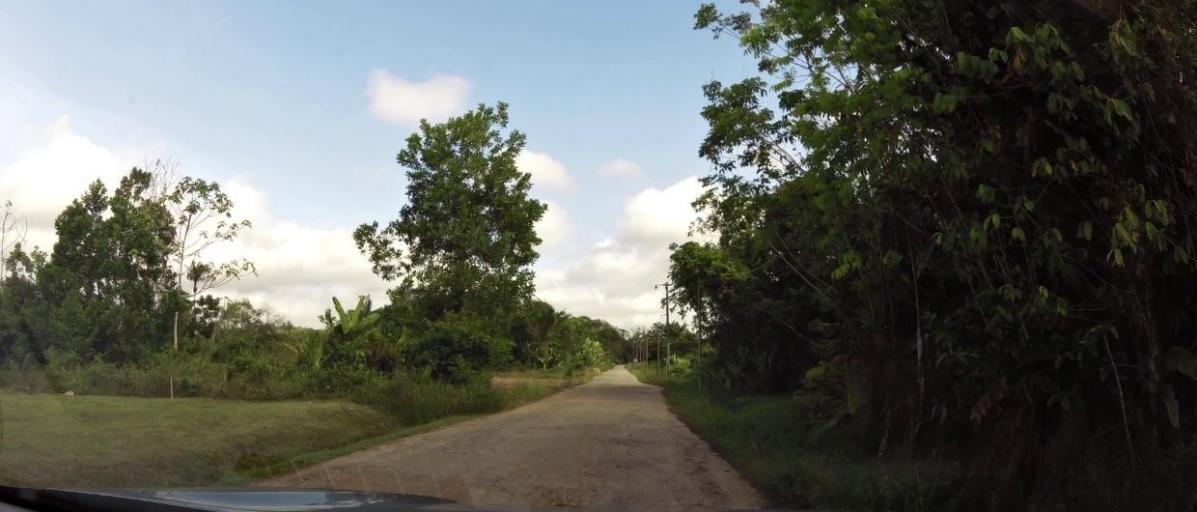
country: GF
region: Guyane
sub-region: Guyane
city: Roura
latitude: 4.7837
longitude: -52.3352
